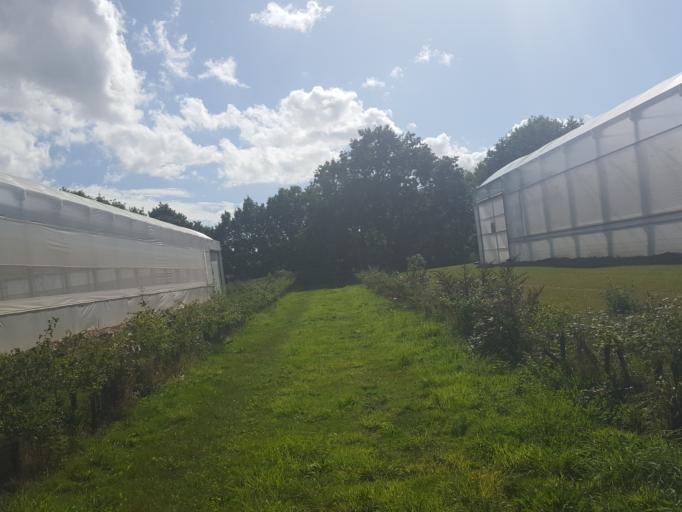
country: GB
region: England
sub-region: Essex
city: Alresford
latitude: 51.8531
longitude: 1.0196
